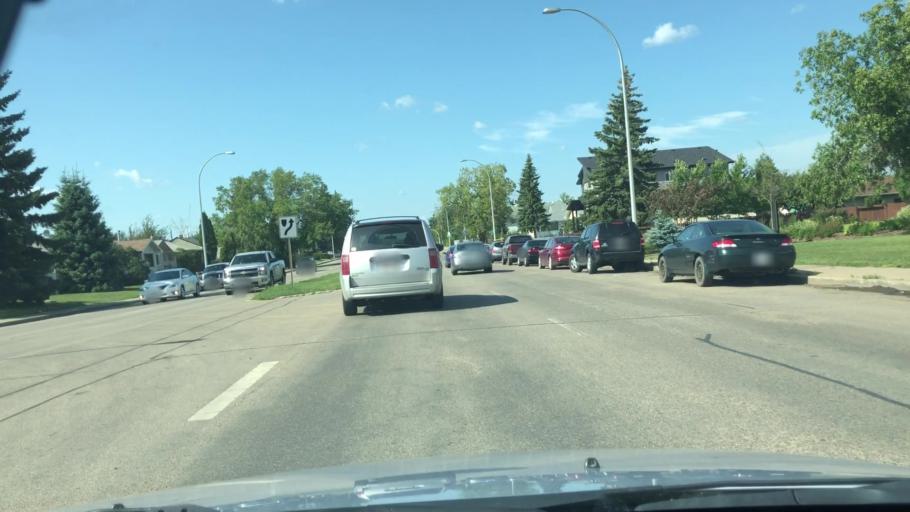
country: CA
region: Alberta
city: Edmonton
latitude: 53.5928
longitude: -113.4429
